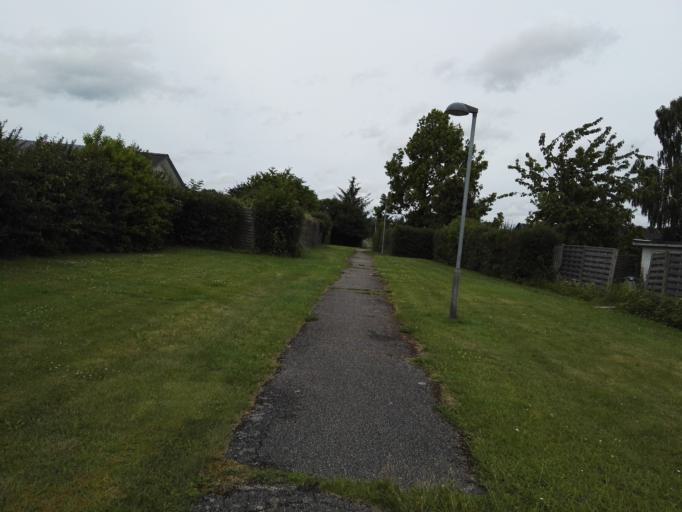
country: DK
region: Capital Region
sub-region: Egedal Kommune
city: Stenlose
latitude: 55.7672
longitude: 12.1690
